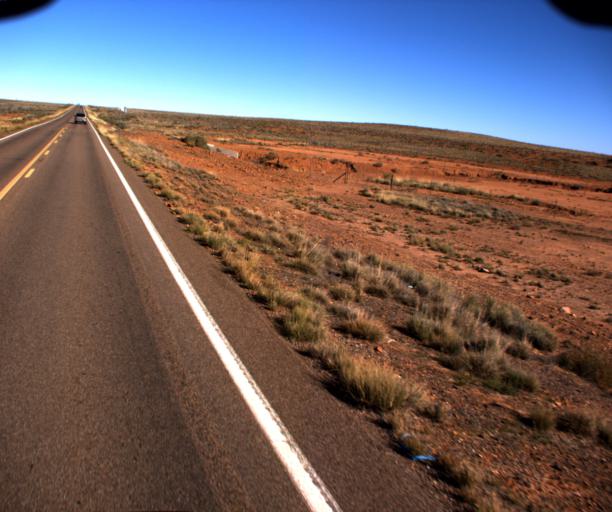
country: US
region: Arizona
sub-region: Navajo County
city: Holbrook
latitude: 34.7757
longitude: -110.1287
